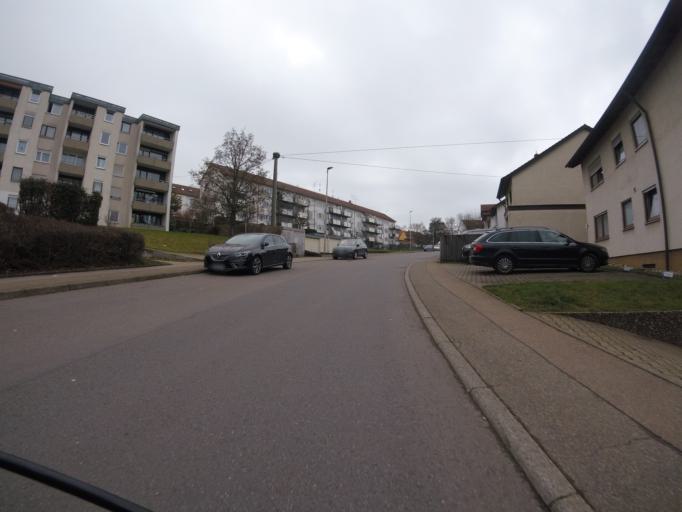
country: DE
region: Baden-Wuerttemberg
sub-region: Regierungsbezirk Stuttgart
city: Backnang
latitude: 48.9499
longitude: 9.4431
